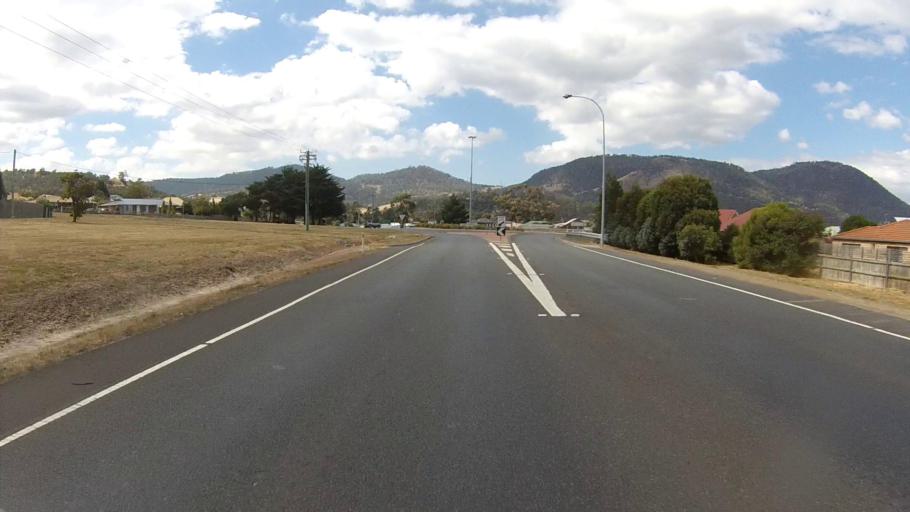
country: AU
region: Tasmania
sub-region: Brighton
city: Old Beach
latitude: -42.7784
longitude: 147.2750
